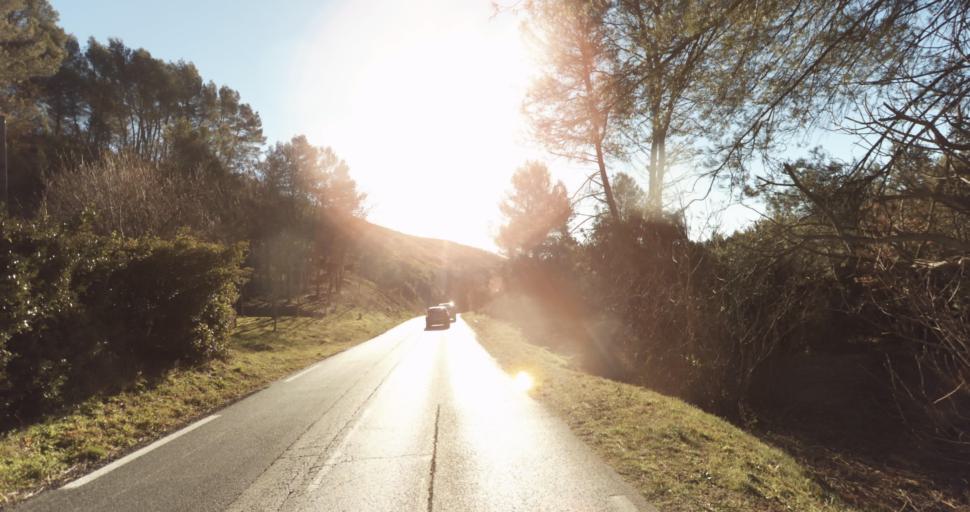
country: FR
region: Provence-Alpes-Cote d'Azur
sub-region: Departement des Bouches-du-Rhone
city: Cadolive
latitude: 43.4070
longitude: 5.5557
